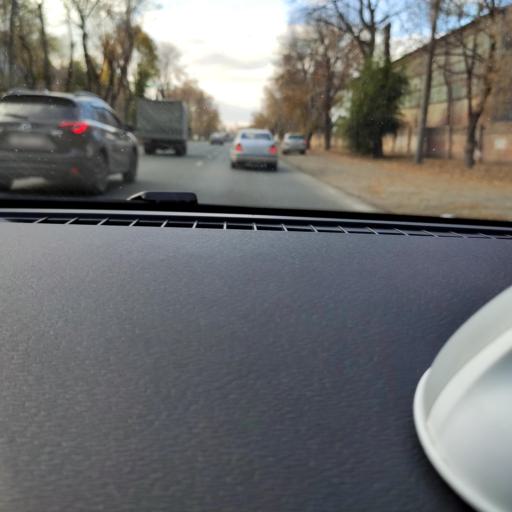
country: RU
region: Samara
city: Smyshlyayevka
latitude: 53.2288
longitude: 50.2928
